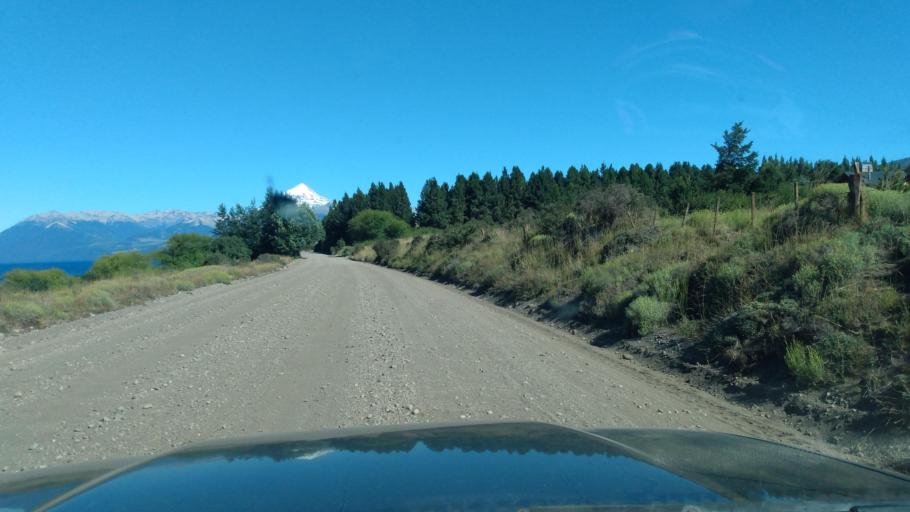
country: AR
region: Neuquen
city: Junin de los Andes
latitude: -39.7868
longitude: -71.2228
